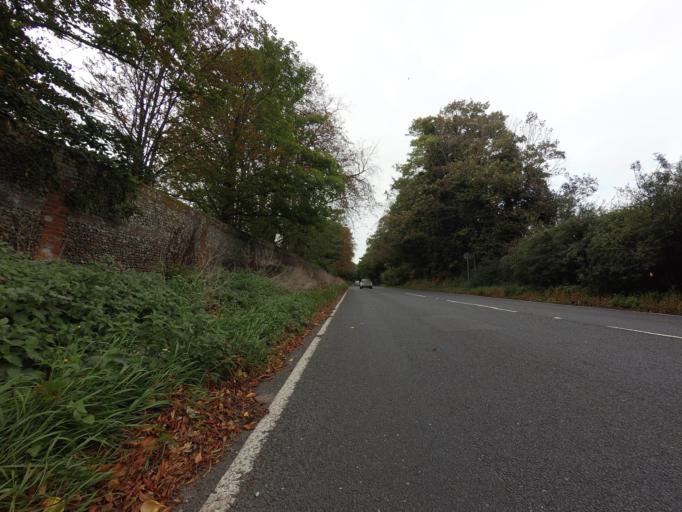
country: GB
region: England
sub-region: Essex
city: Saffron Walden
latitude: 52.0272
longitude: 0.2330
